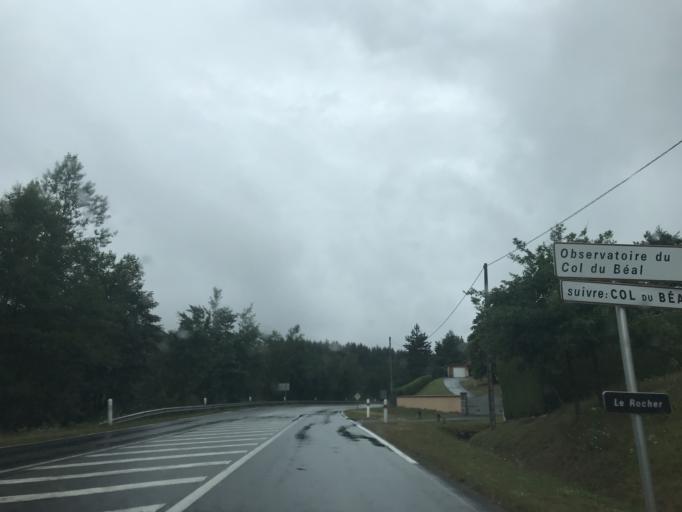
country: FR
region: Auvergne
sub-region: Departement du Puy-de-Dome
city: Job
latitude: 45.6289
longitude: 3.7133
